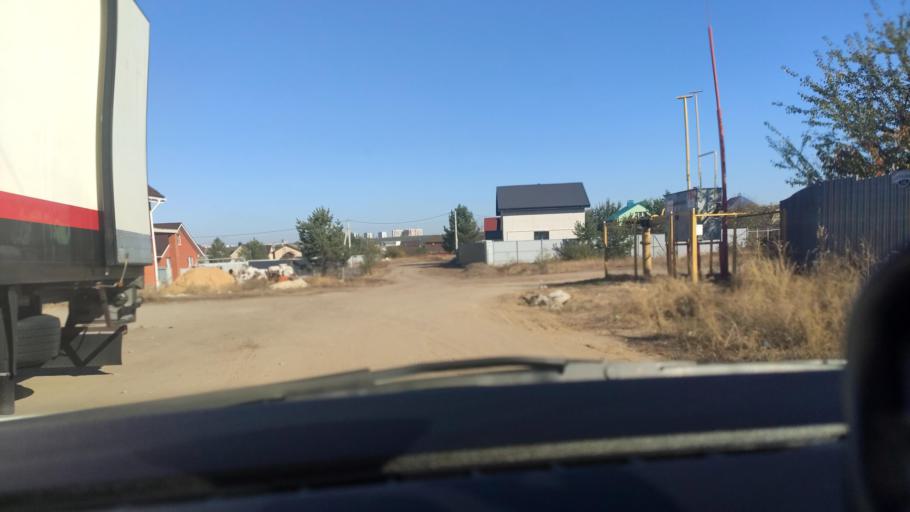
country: RU
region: Voronezj
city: Pridonskoy
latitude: 51.6319
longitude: 39.0969
